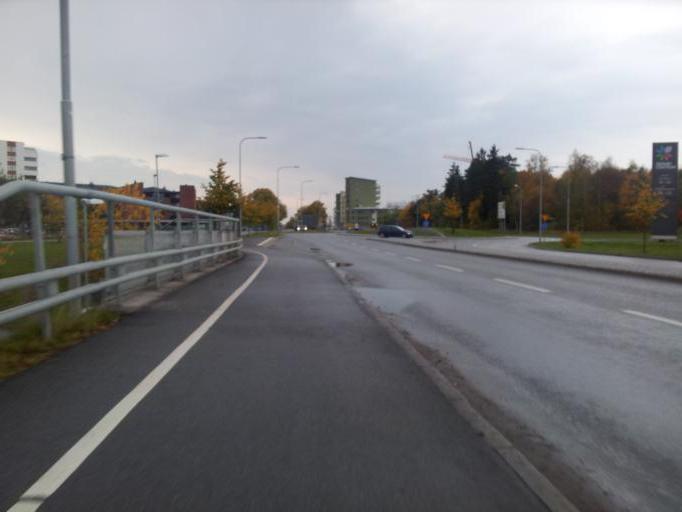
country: SE
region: Uppsala
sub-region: Uppsala Kommun
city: Uppsala
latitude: 59.8752
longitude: 17.6754
